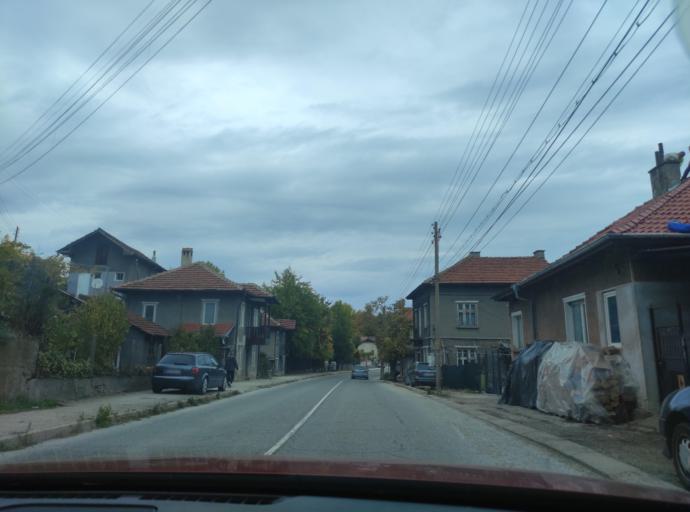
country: BG
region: Montana
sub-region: Obshtina Berkovitsa
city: Berkovitsa
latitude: 43.2014
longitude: 23.1616
